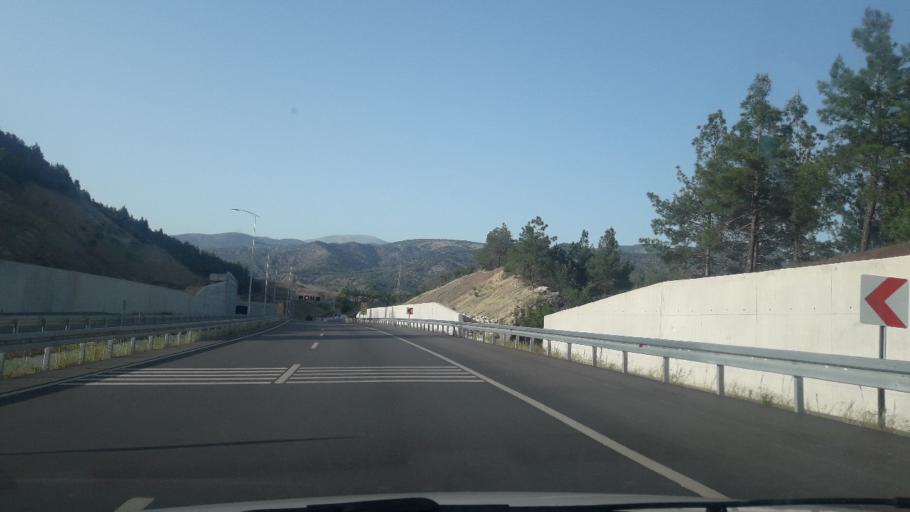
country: TR
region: Amasya
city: Amasya
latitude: 40.6821
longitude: 35.8119
